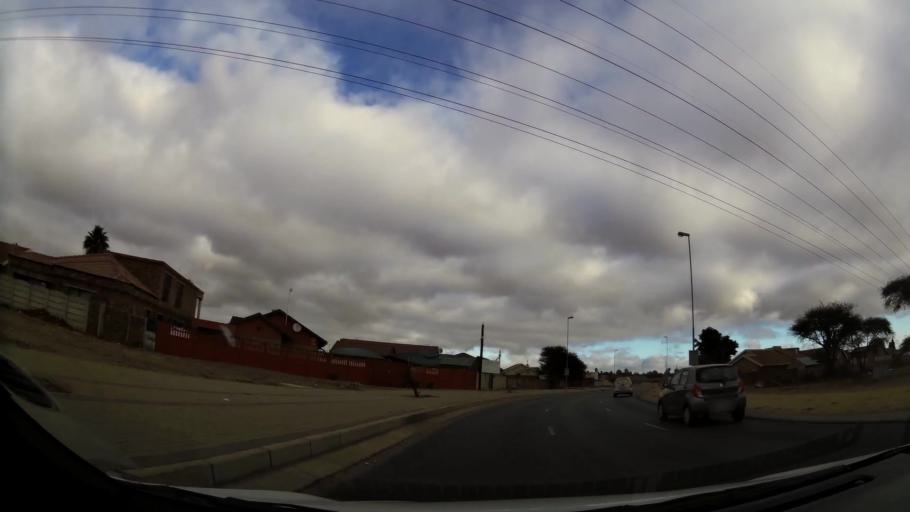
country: ZA
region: Limpopo
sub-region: Capricorn District Municipality
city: Polokwane
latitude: -23.9211
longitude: 29.4508
